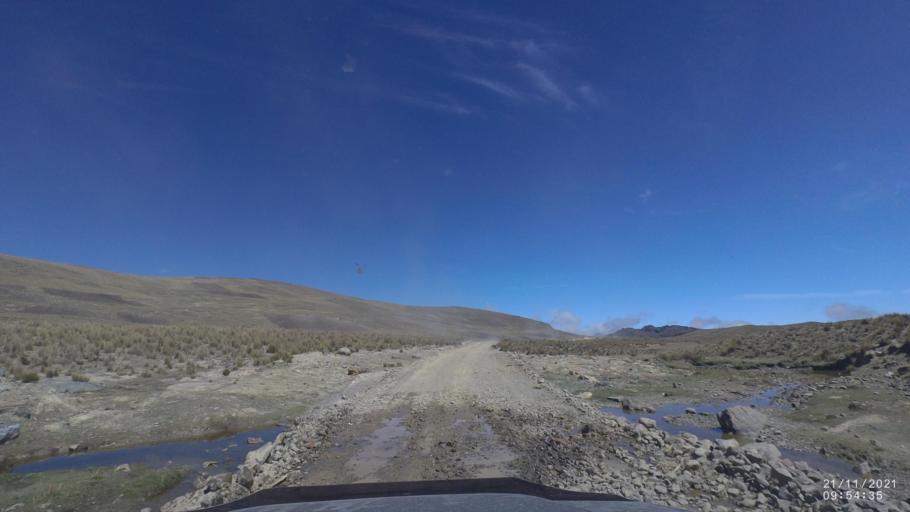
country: BO
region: Cochabamba
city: Cochabamba
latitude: -17.0526
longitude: -66.2615
